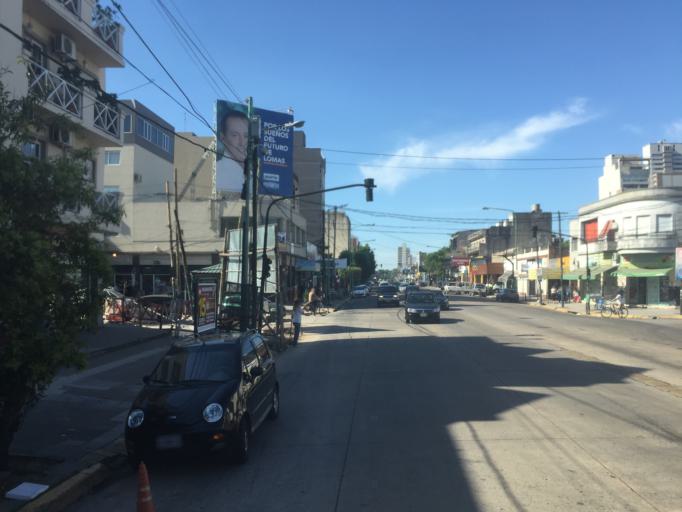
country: AR
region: Buenos Aires
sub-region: Partido de Lomas de Zamora
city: Lomas de Zamora
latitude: -34.7459
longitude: -58.3937
